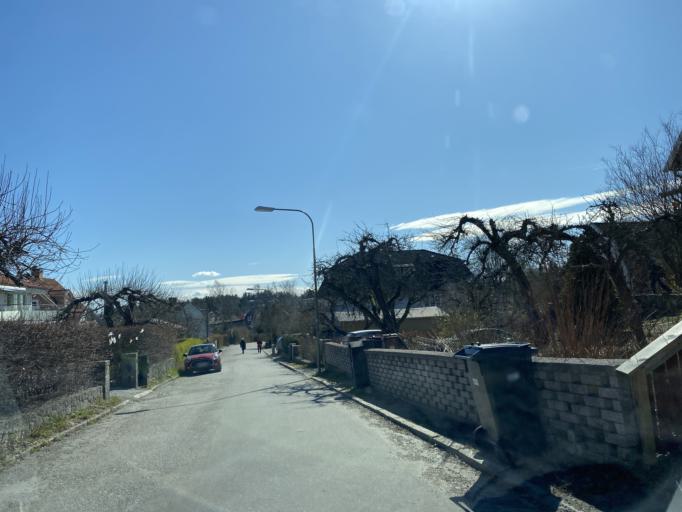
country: SE
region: Stockholm
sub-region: Stockholms Kommun
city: Arsta
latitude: 59.2812
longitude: 18.0556
